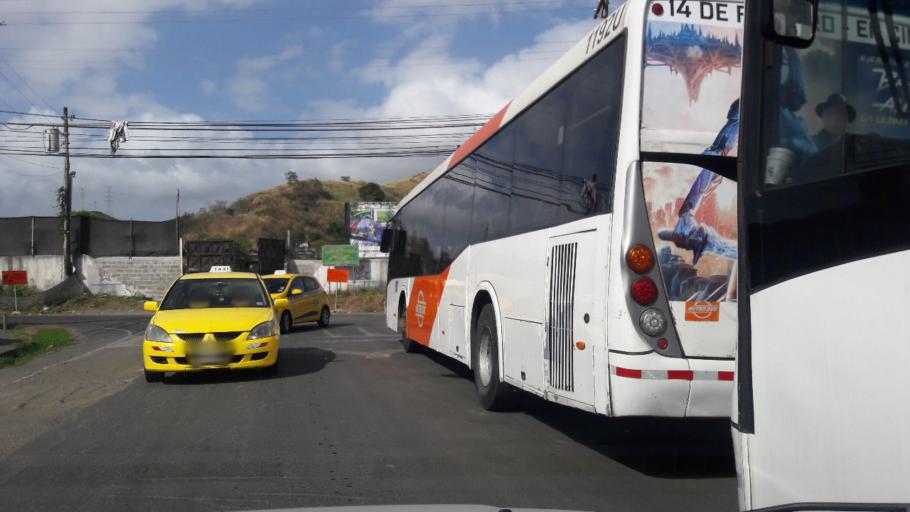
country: PA
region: Panama
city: San Miguelito
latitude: 9.0495
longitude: -79.5102
